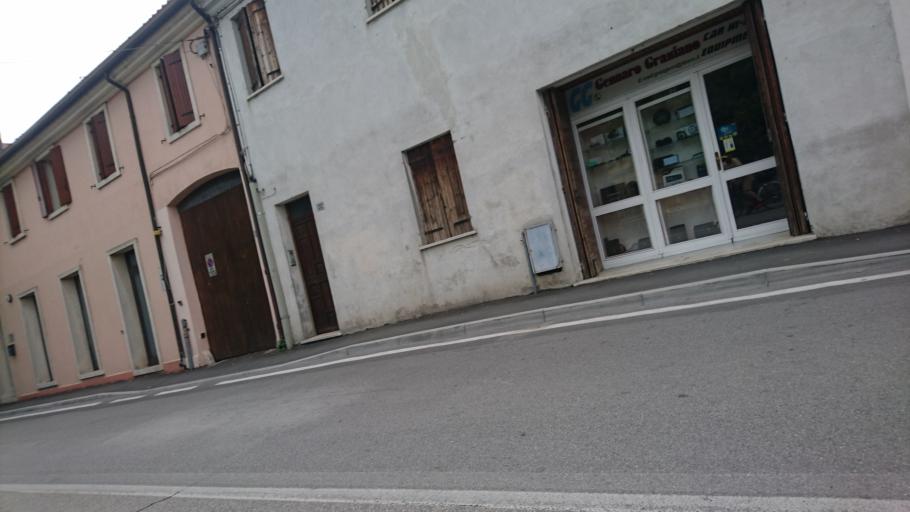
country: IT
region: Veneto
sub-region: Provincia di Rovigo
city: Badia Polesine
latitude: 45.0954
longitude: 11.4940
